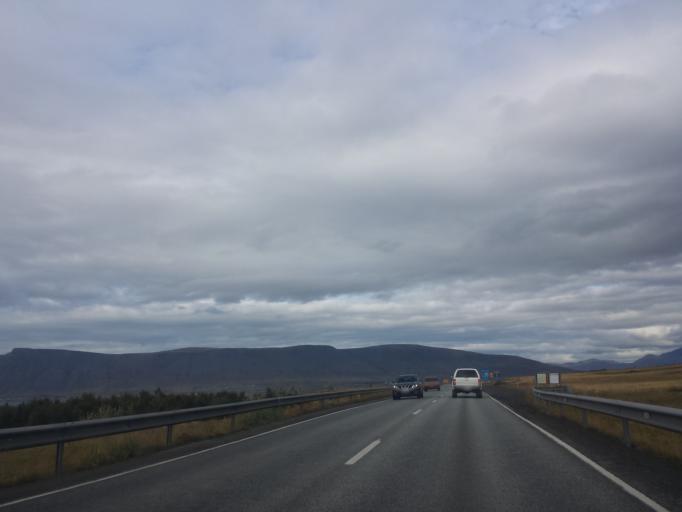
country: IS
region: Capital Region
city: Reykjavik
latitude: 64.2686
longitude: -21.8344
